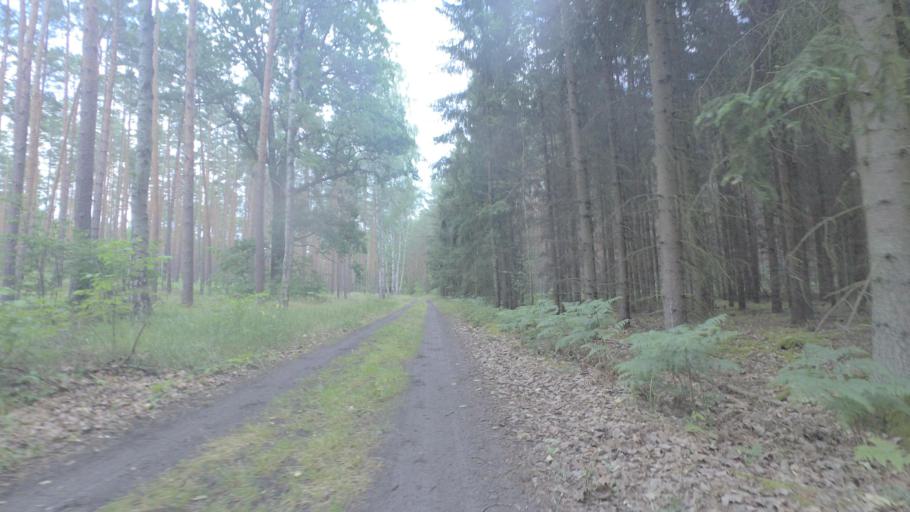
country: DE
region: Brandenburg
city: Am Mellensee
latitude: 52.1275
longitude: 13.4416
